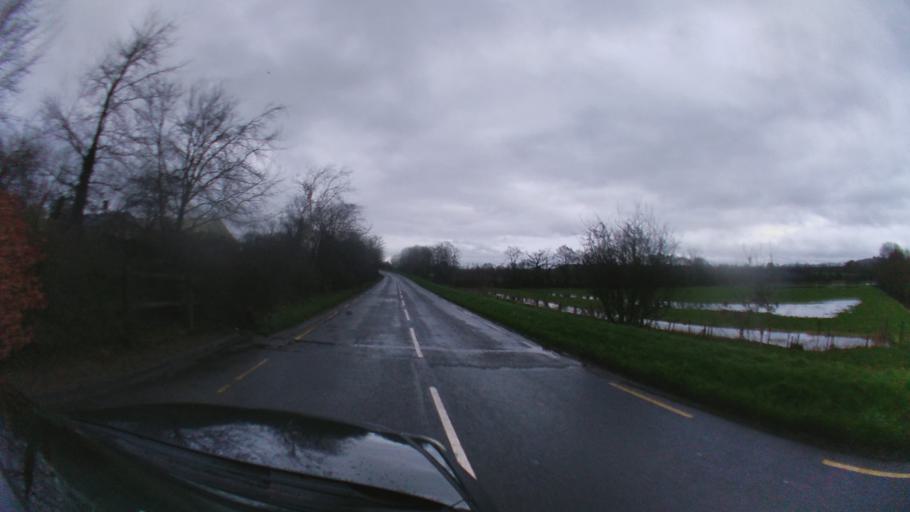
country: IE
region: Leinster
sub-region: County Carlow
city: Bagenalstown
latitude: 52.6356
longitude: -6.9942
